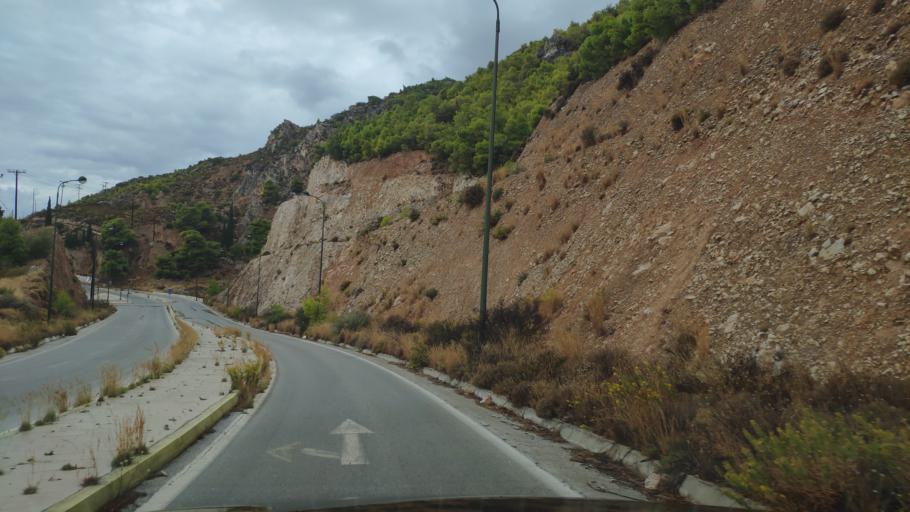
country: GR
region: Peloponnese
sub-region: Nomos Korinthias
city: Loutraki
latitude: 37.9822
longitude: 22.9789
